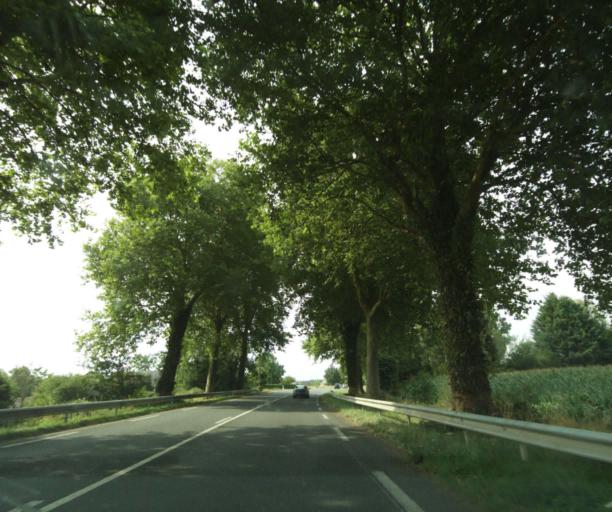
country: FR
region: Pays de la Loire
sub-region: Departement de la Sarthe
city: Mulsanne
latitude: 47.8913
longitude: 0.2439
